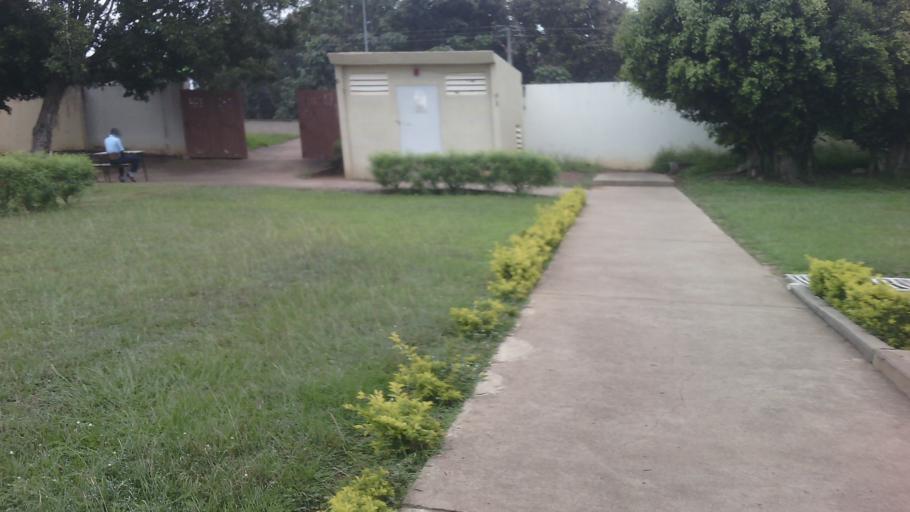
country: CI
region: Vallee du Bandama
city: Bouake
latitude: 7.6851
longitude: -5.0673
